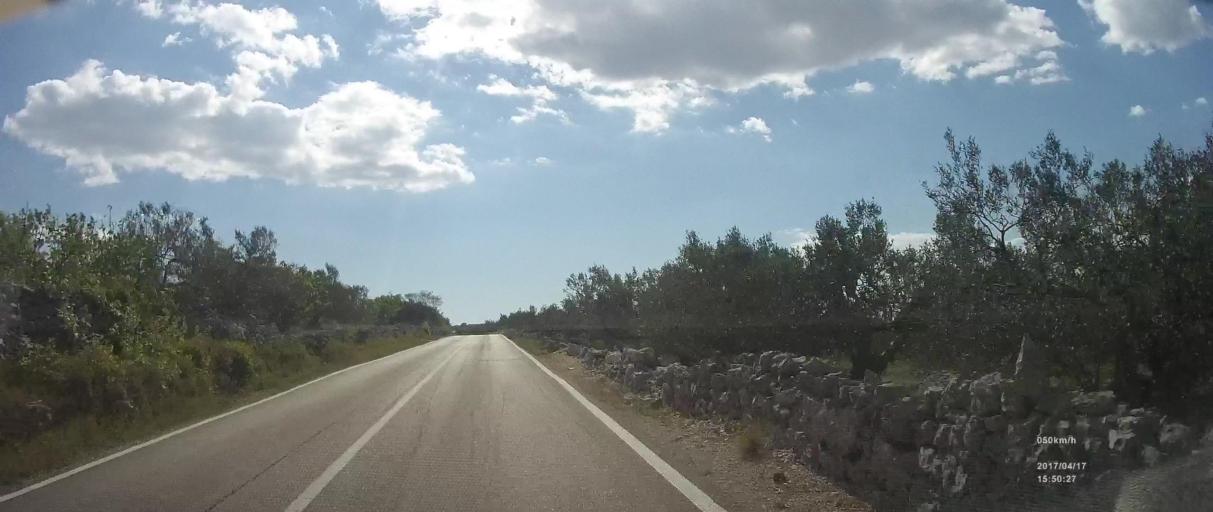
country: HR
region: Sibensko-Kniniska
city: Primosten
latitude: 43.6081
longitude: 15.9723
